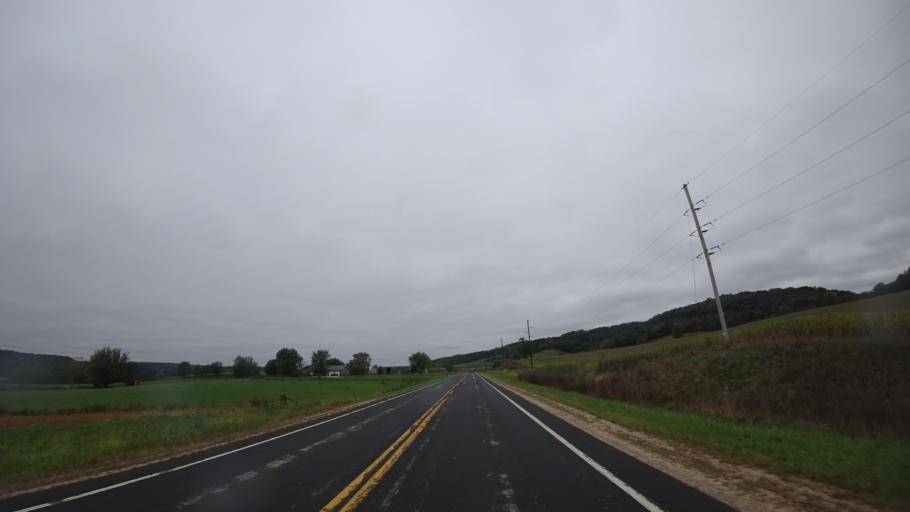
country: US
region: Wisconsin
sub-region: Grant County
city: Boscobel
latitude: 43.1048
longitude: -90.8162
